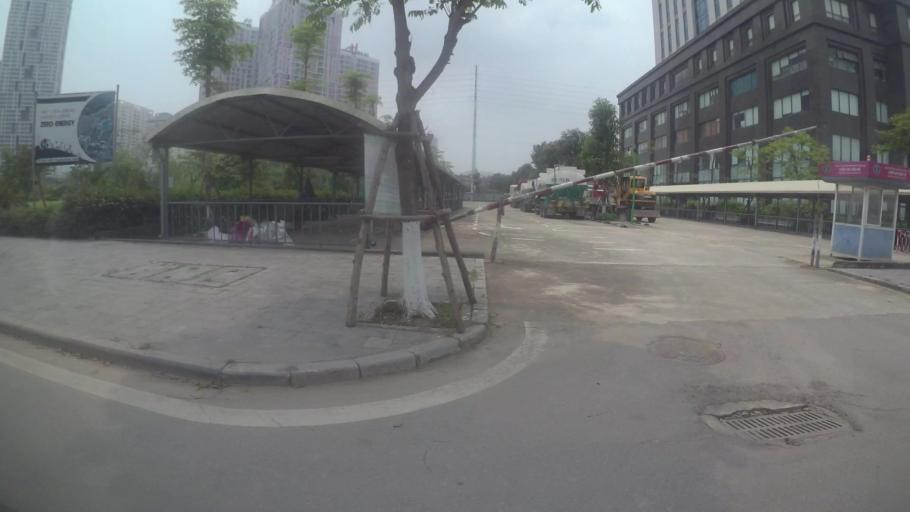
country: VN
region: Ha Noi
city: Ha Dong
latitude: 20.9754
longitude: 105.7583
